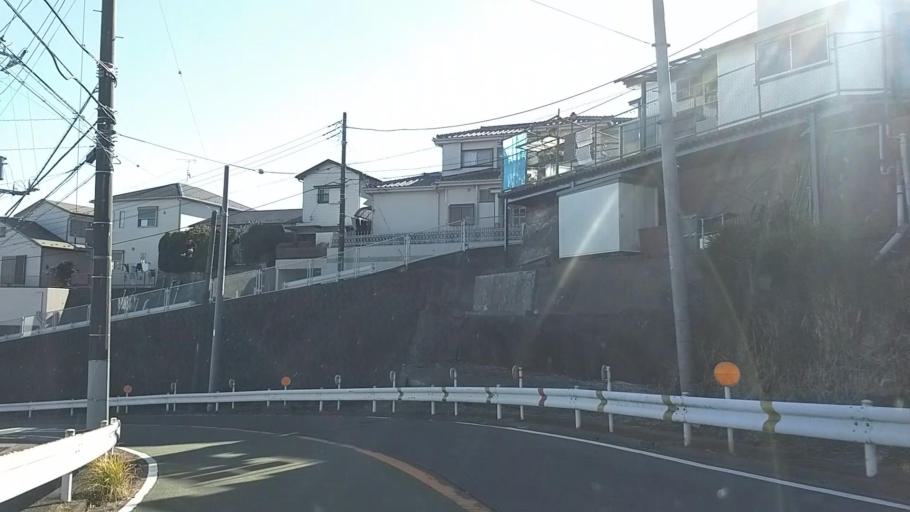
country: JP
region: Kanagawa
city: Yokohama
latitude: 35.4506
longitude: 139.5818
